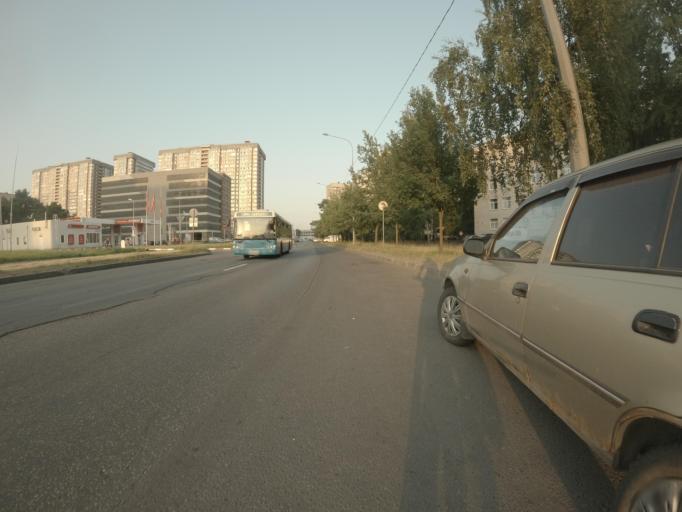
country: RU
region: St.-Petersburg
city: Krasnogvargeisky
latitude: 59.9772
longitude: 30.4322
